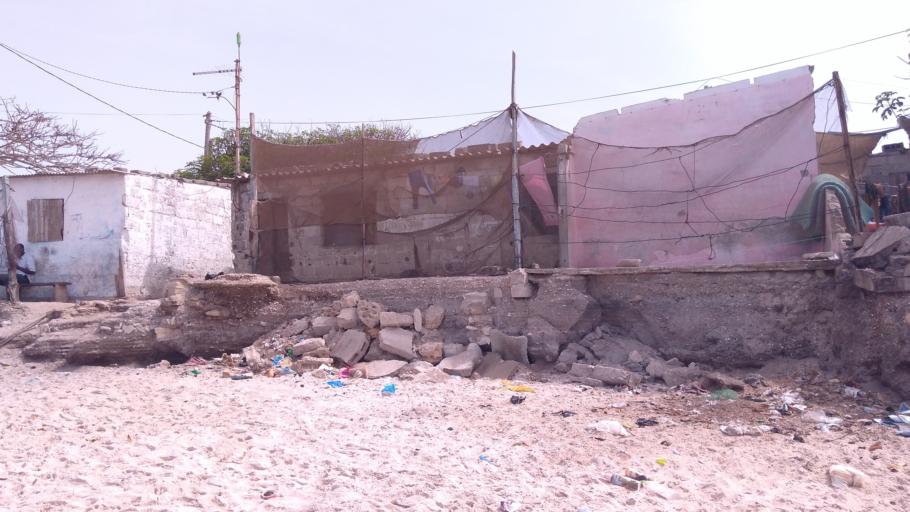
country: SN
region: Dakar
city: Pikine
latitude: 14.6868
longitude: -17.2294
